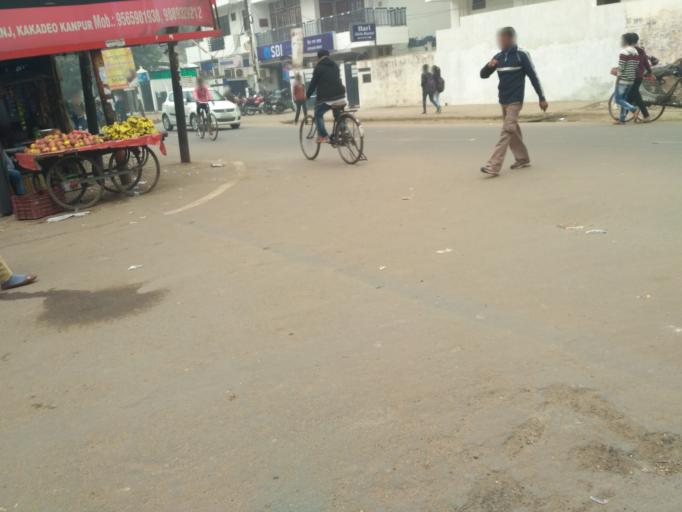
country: IN
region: Uttar Pradesh
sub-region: Kanpur
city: Nawabganj
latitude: 26.4810
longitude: 80.2916
